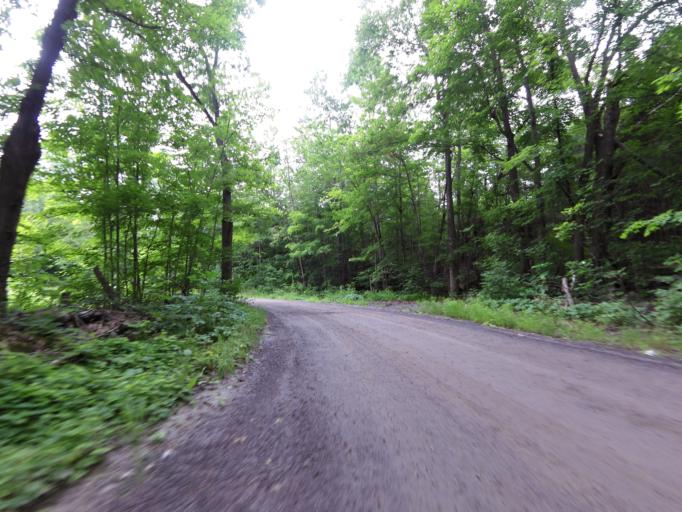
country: CA
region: Ontario
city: Perth
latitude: 44.7125
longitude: -76.6272
